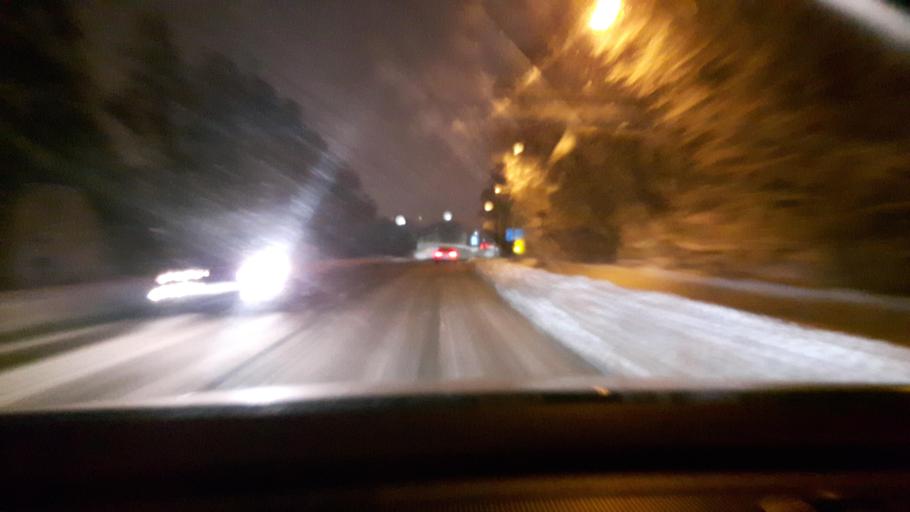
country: SE
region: Vaestra Goetaland
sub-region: Goteborg
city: Majorna
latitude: 57.6698
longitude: 11.8868
